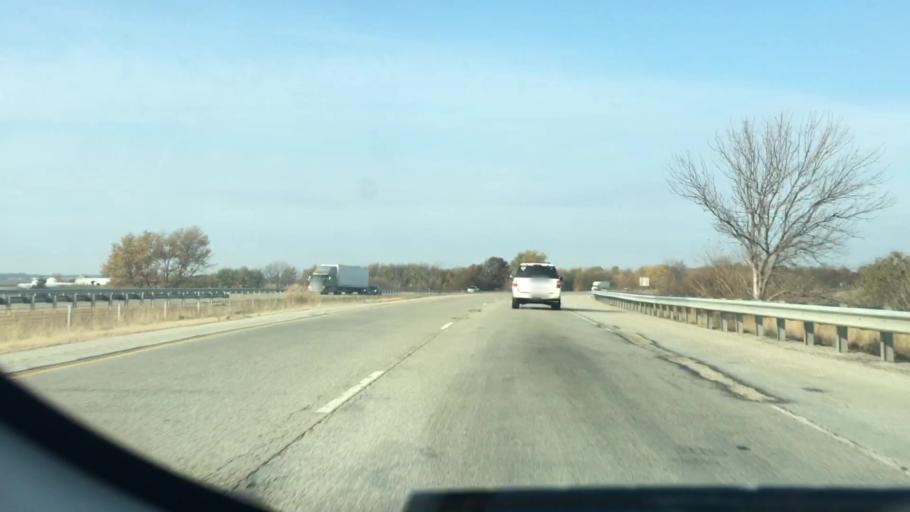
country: US
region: Illinois
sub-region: McLean County
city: Twin Grove
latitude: 40.5405
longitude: -89.0730
